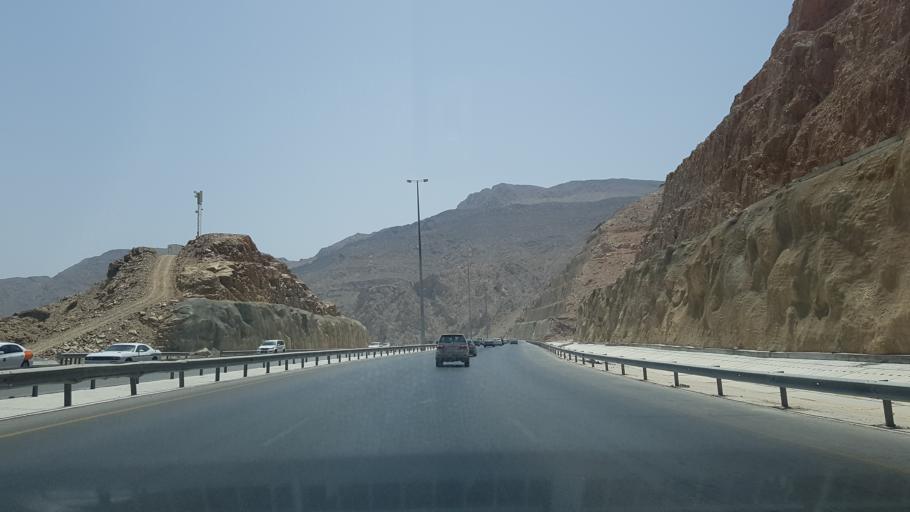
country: OM
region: Muhafazat Masqat
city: Muscat
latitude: 23.5716
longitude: 58.5250
